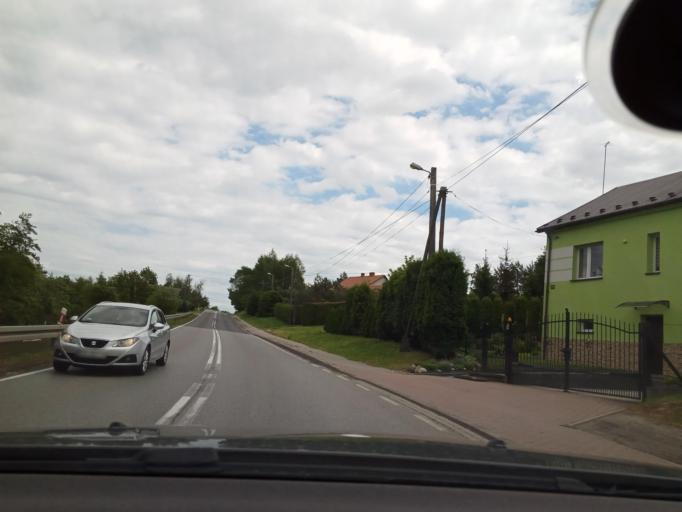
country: PL
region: Lesser Poland Voivodeship
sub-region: Powiat wielicki
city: Trabki
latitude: 49.9546
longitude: 20.1540
